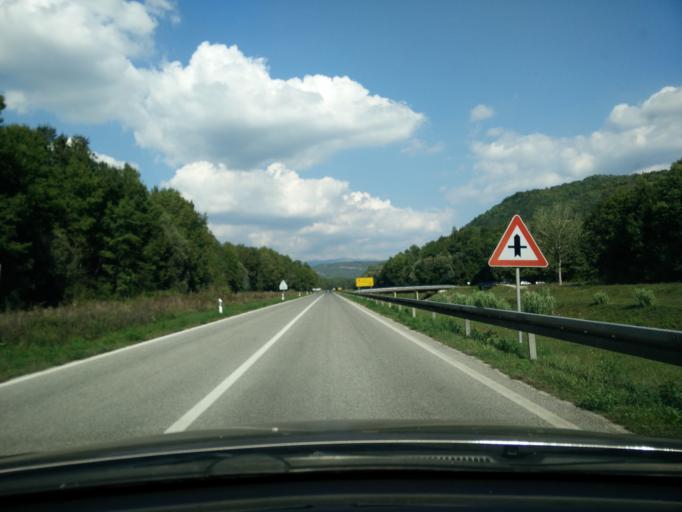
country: HR
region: Istarska
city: Karojba
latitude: 45.3572
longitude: 13.8570
